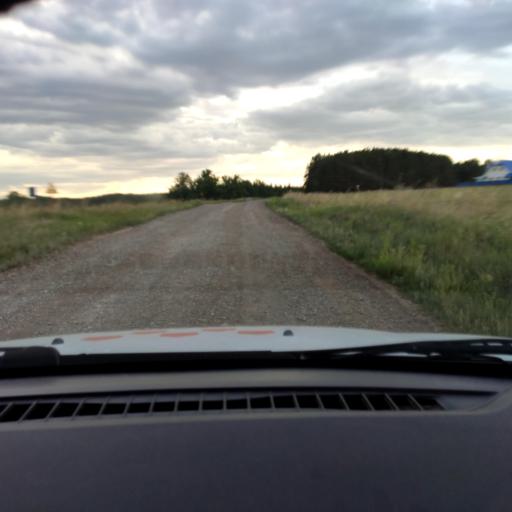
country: RU
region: Bashkortostan
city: Chishmy
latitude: 54.6112
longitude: 55.3952
